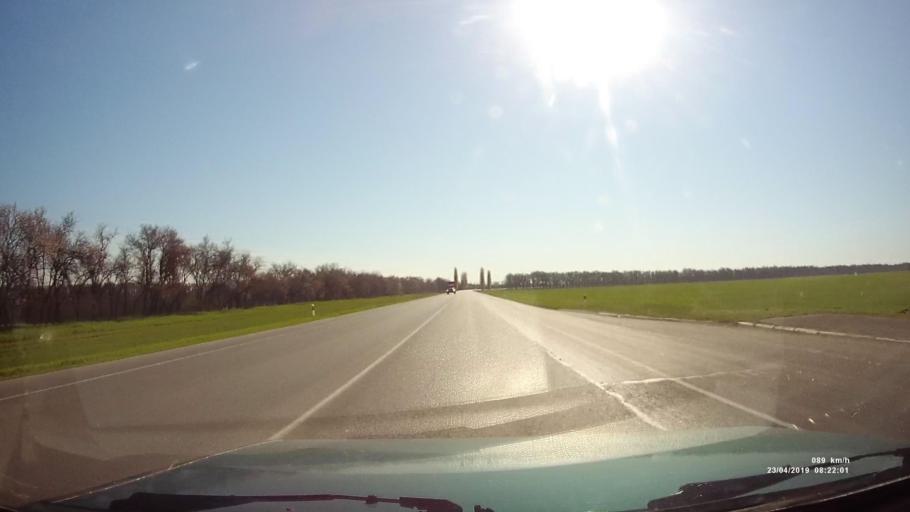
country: RU
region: Rostov
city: Tselina
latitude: 46.5373
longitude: 40.9024
